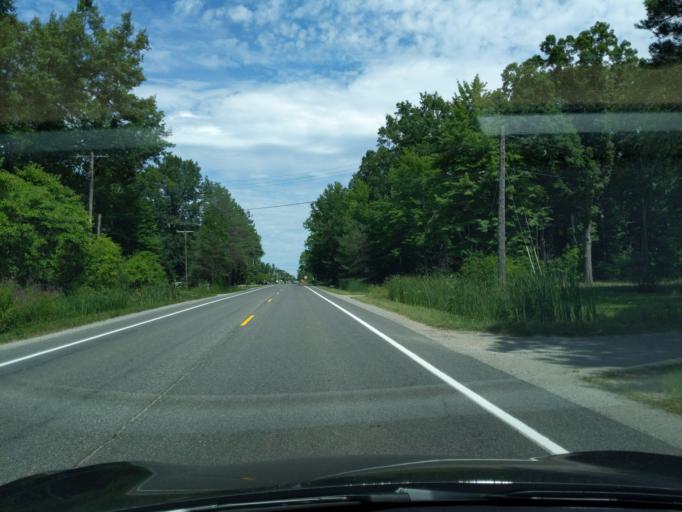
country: US
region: Michigan
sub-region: Midland County
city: Midland
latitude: 43.6076
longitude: -84.3692
